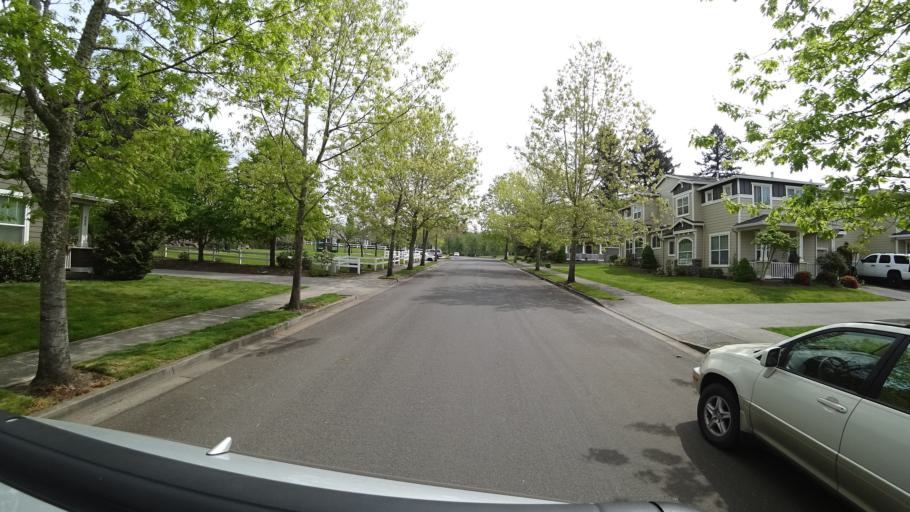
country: US
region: Oregon
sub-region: Washington County
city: Hillsboro
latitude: 45.5351
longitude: -122.9963
